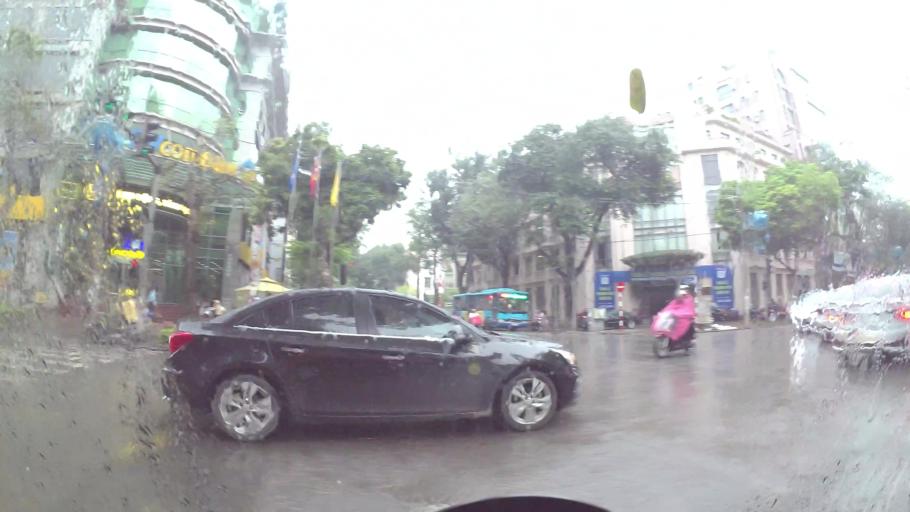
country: VN
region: Ha Noi
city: Hoan Kiem
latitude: 21.0237
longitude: 105.8546
